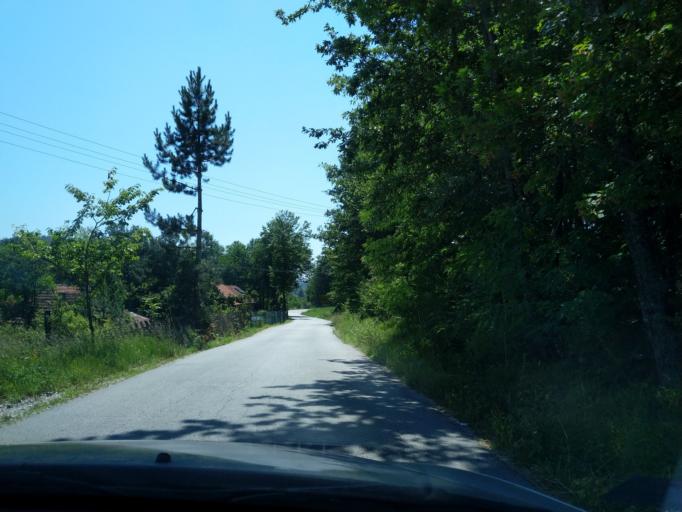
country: RS
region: Central Serbia
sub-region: Zlatiborski Okrug
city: Uzice
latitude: 43.7836
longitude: 19.8561
